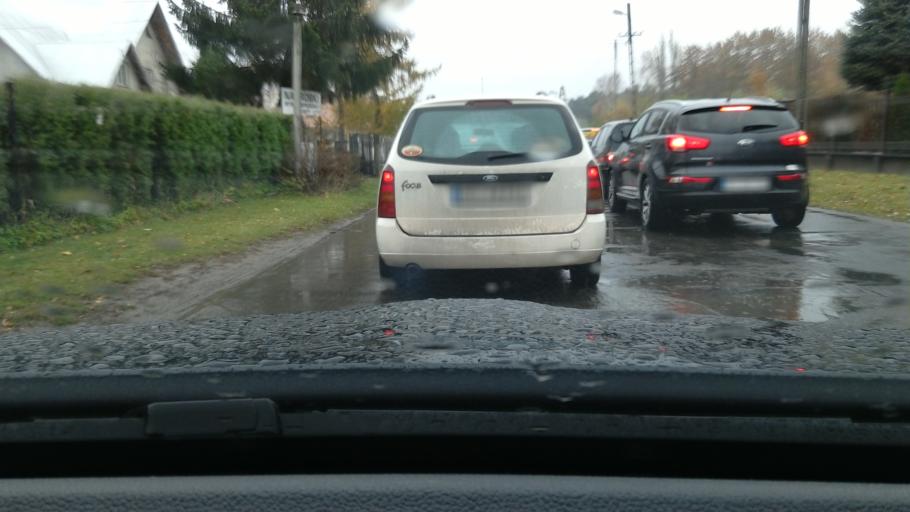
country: PL
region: Lodz Voivodeship
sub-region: Skierniewice
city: Skierniewice
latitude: 51.9408
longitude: 20.1548
